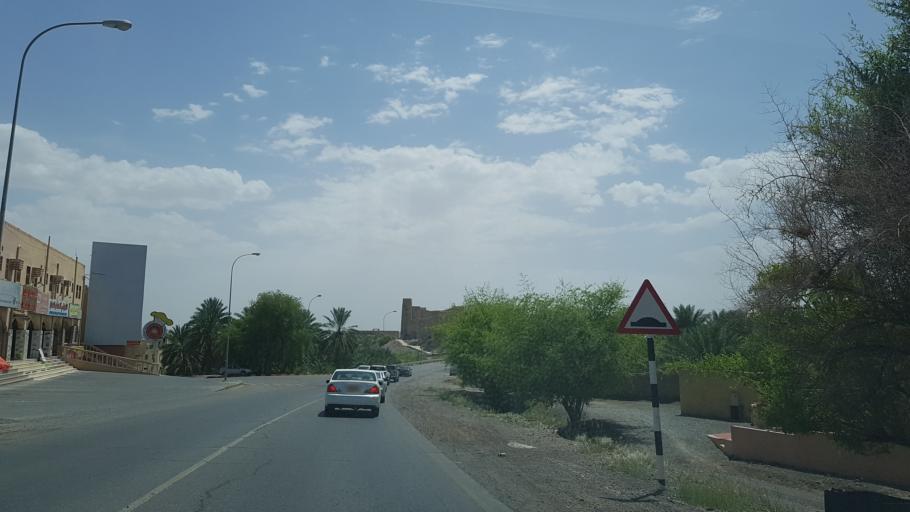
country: OM
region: Muhafazat ad Dakhiliyah
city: Bahla'
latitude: 22.9680
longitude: 57.3022
